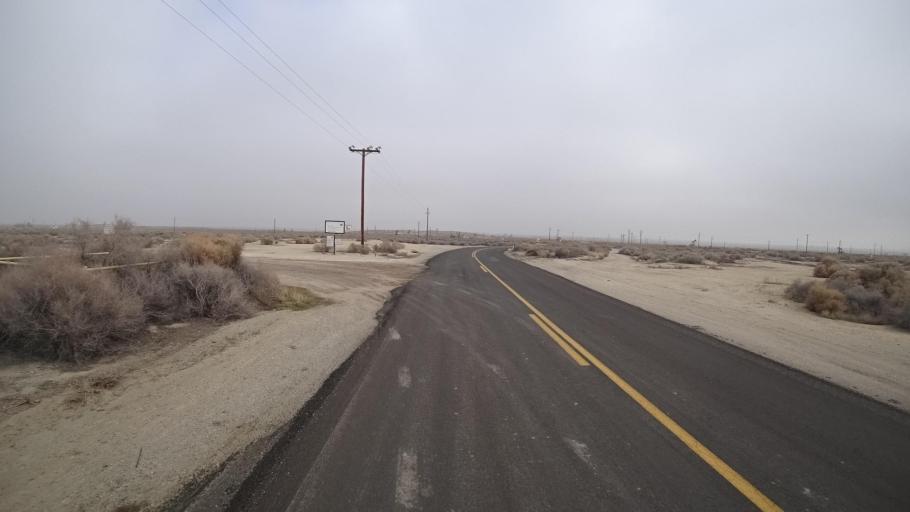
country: US
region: California
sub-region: Kern County
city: Maricopa
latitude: 35.0772
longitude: -119.3697
